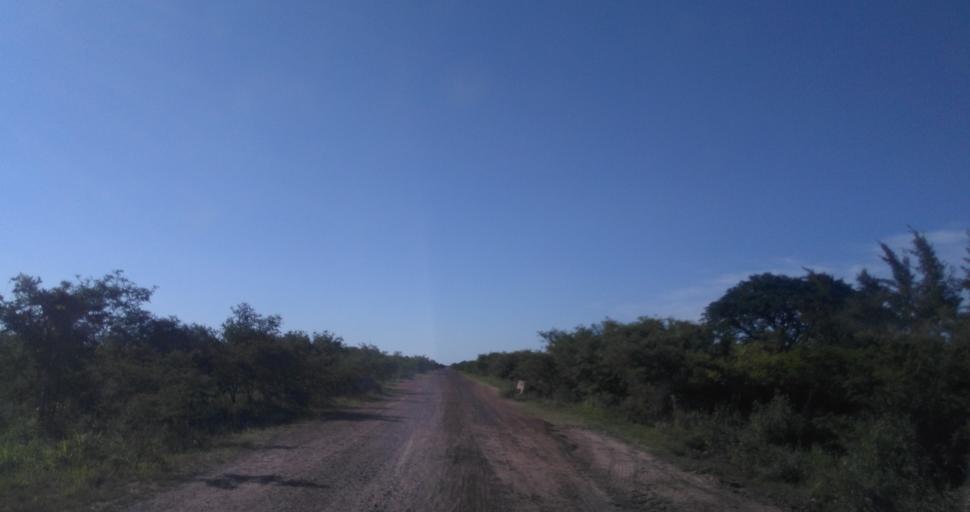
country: AR
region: Chaco
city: Barranqueras
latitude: -27.4254
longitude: -58.9292
